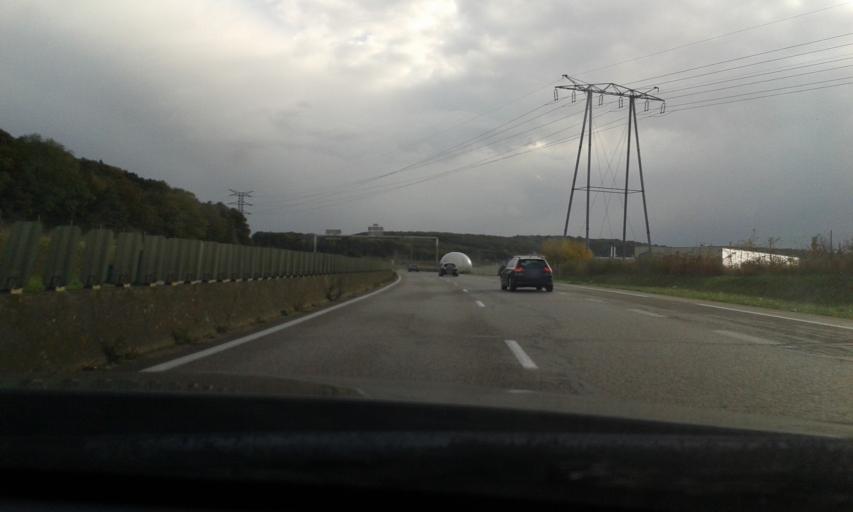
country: FR
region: Haute-Normandie
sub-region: Departement de l'Eure
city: Gravigny
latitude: 49.0580
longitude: 1.1745
